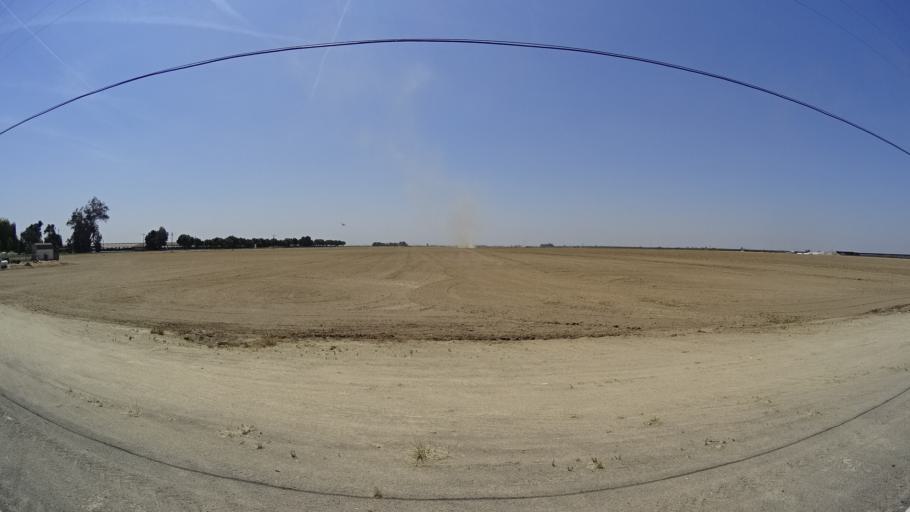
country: US
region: California
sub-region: Fresno County
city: Kingsburg
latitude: 36.4015
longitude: -119.5307
